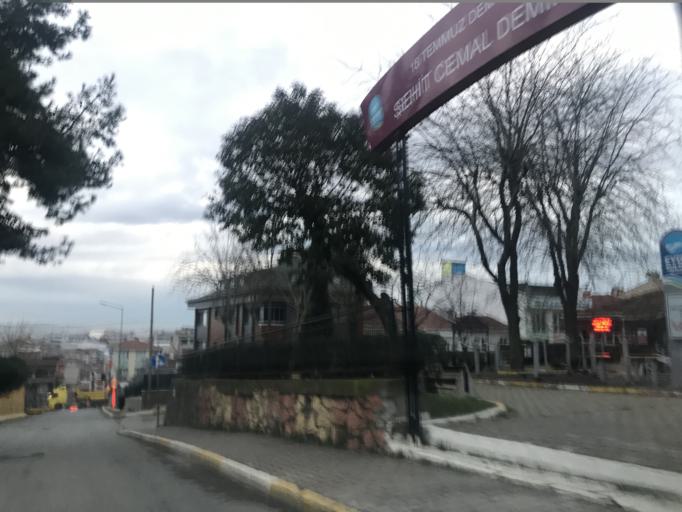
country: TR
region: Istanbul
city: Istanbul
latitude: 41.0417
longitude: 28.9242
